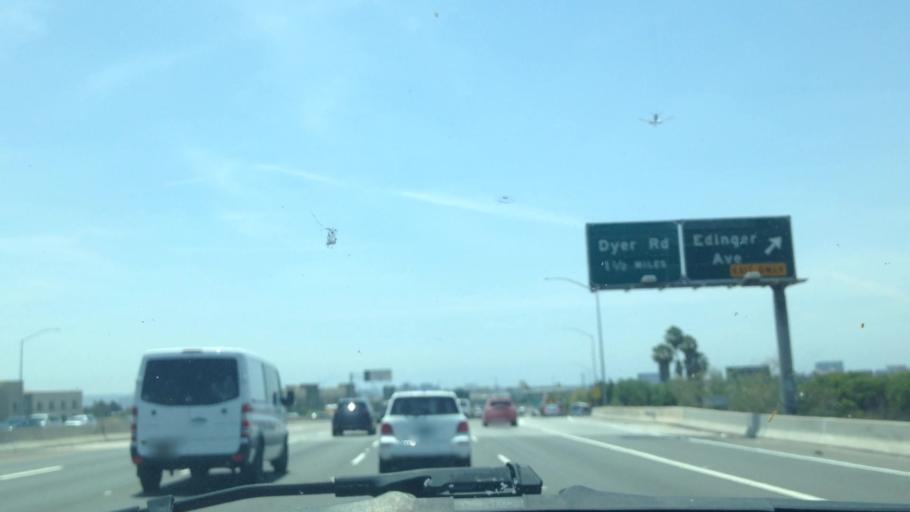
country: US
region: California
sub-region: Orange County
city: Tustin
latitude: 33.7274
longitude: -117.8348
